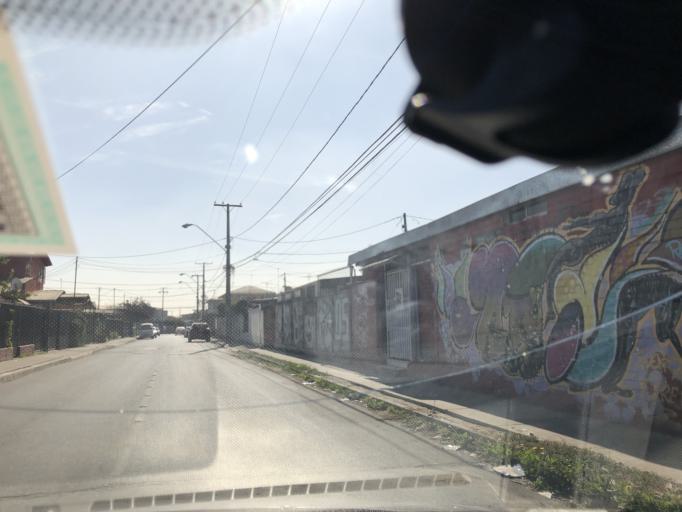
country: CL
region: Santiago Metropolitan
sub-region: Provincia de Cordillera
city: Puente Alto
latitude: -33.5892
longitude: -70.5993
